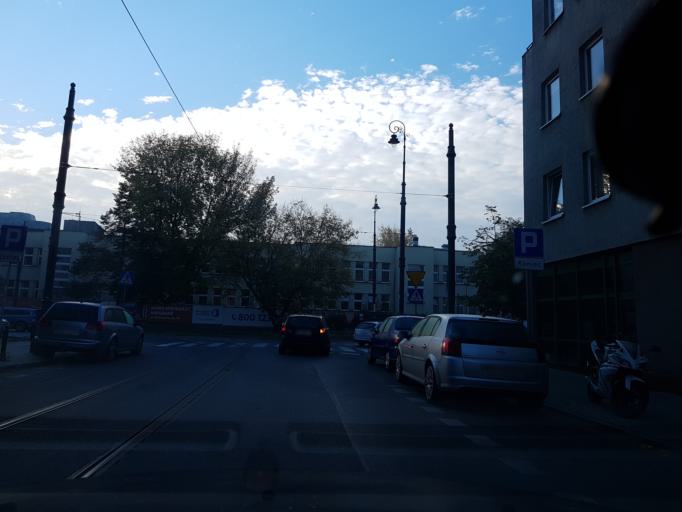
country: PL
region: Masovian Voivodeship
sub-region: Warszawa
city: Praga Polnoc
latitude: 52.2593
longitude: 21.0413
